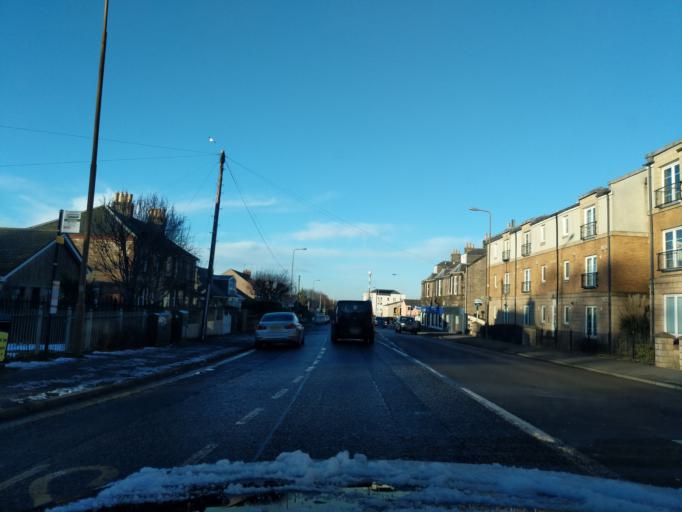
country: GB
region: Scotland
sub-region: West Lothian
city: Seafield
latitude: 55.9341
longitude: -3.1142
